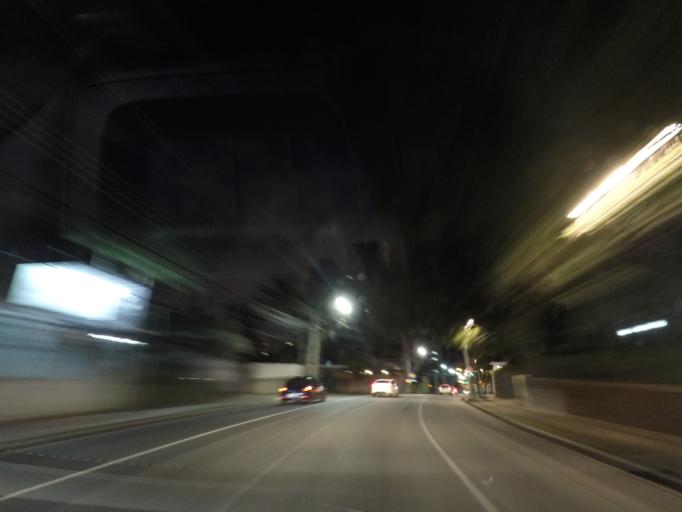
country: BR
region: Parana
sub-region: Curitiba
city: Curitiba
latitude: -25.4179
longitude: -49.2661
